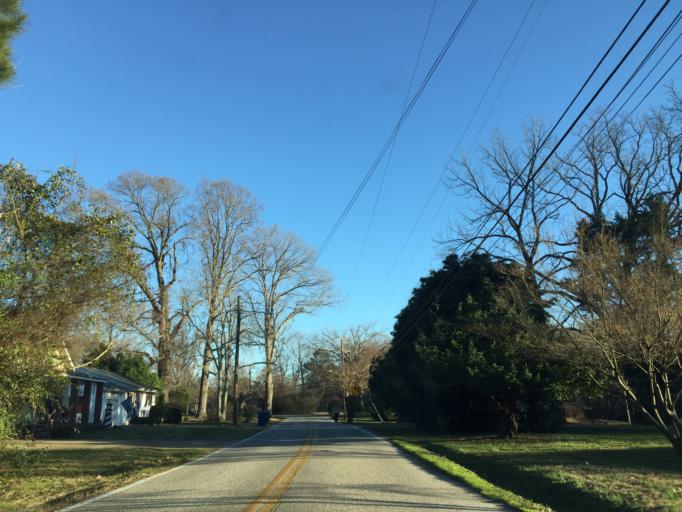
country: US
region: Virginia
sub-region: Isle of Wight County
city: Carrollton
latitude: 37.0790
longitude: -76.5235
